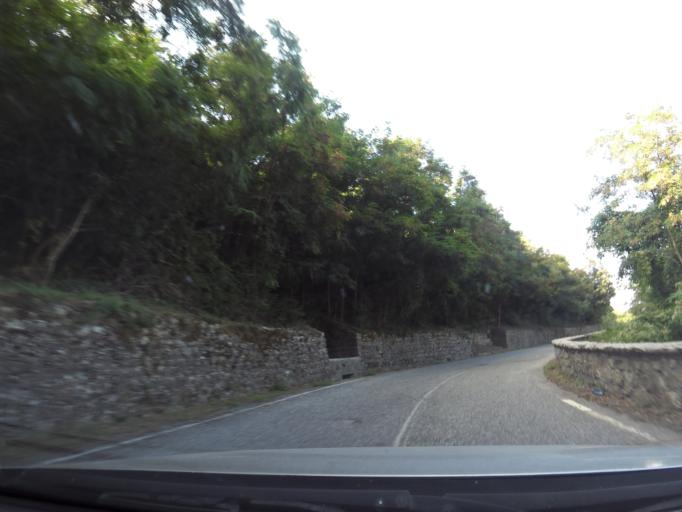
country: IT
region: Calabria
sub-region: Provincia di Reggio Calabria
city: Pazzano
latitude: 38.4635
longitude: 16.4233
